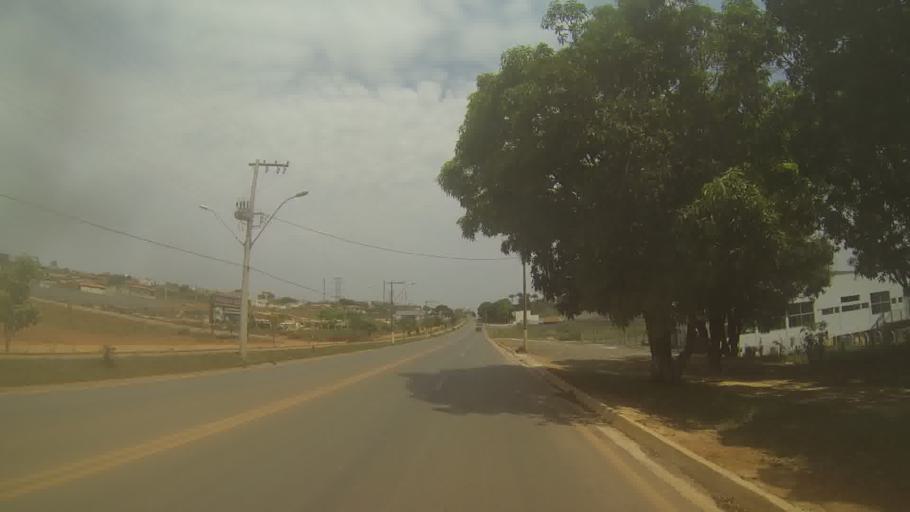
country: BR
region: Minas Gerais
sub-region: Bambui
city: Bambui
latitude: -20.0155
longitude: -45.9621
